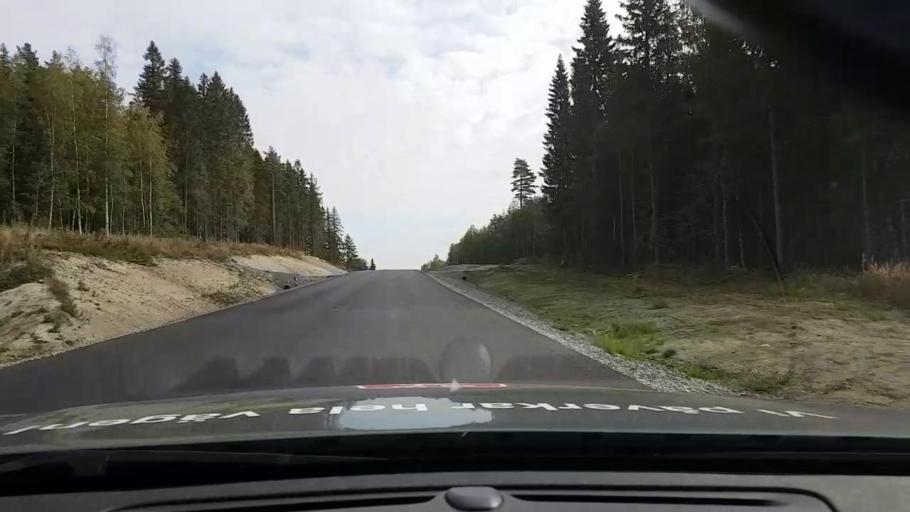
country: SE
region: Vaesternorrland
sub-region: OErnskoeldsviks Kommun
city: Bjasta
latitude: 63.2921
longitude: 18.5032
